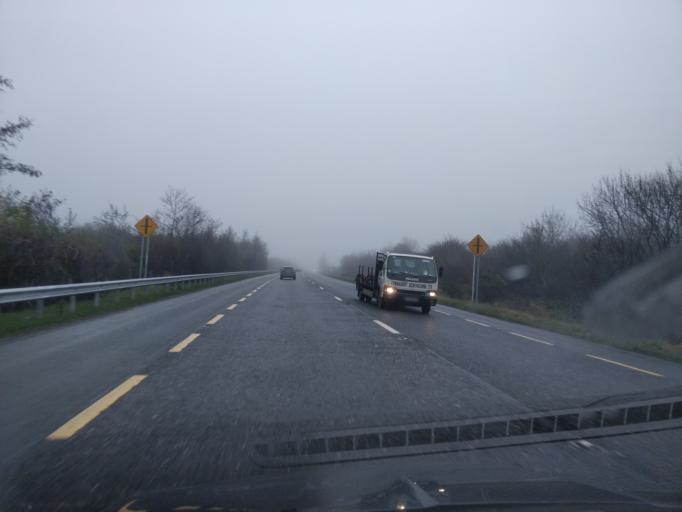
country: IE
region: Connaught
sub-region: Maigh Eo
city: Castlebar
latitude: 53.8777
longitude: -9.2277
